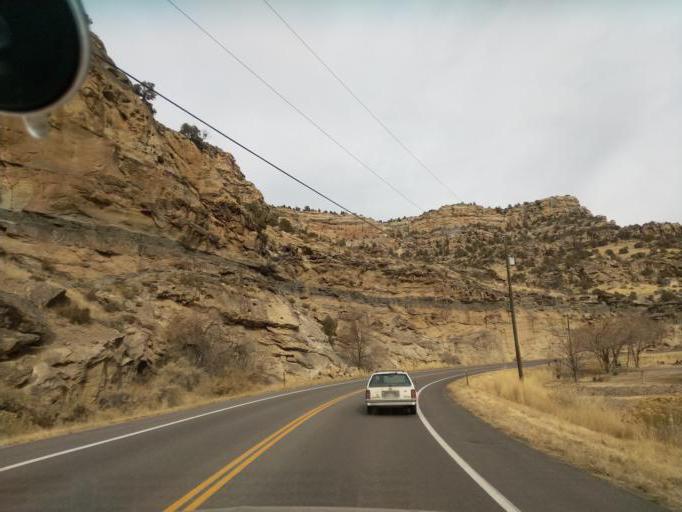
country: US
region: Colorado
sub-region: Mesa County
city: Palisade
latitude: 39.1908
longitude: -108.2588
